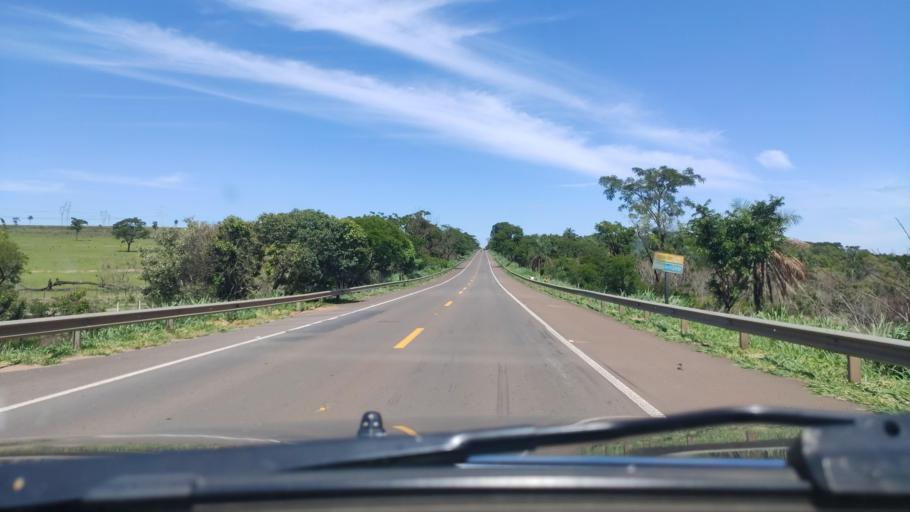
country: BR
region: Sao Paulo
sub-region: Sao Carlos
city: Sao Carlos
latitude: -22.0662
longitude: -47.9131
